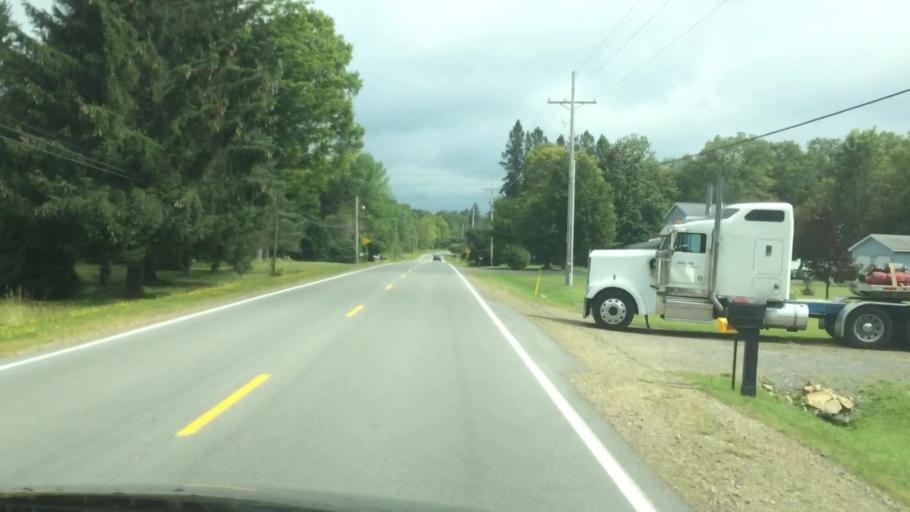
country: US
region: Pennsylvania
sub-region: McKean County
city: Bradford
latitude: 41.8689
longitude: -78.5914
